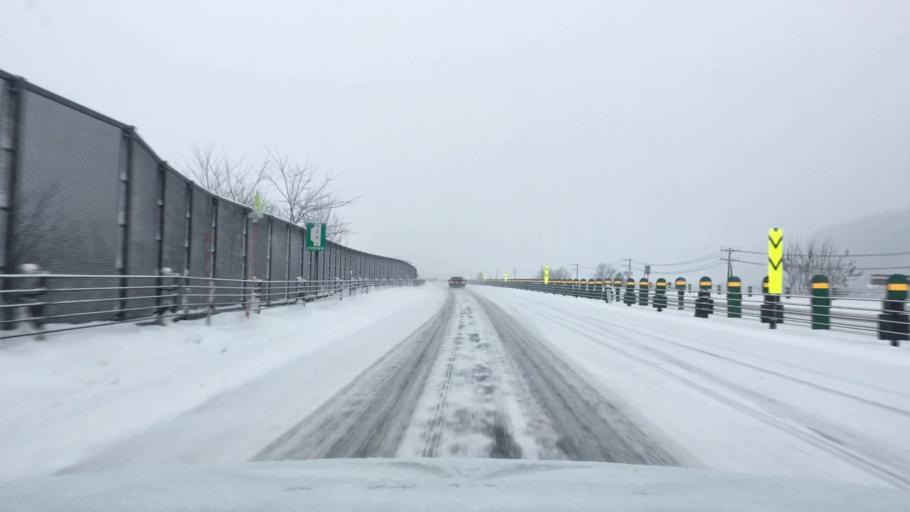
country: JP
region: Akita
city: Hanawa
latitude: 40.2781
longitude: 140.7613
